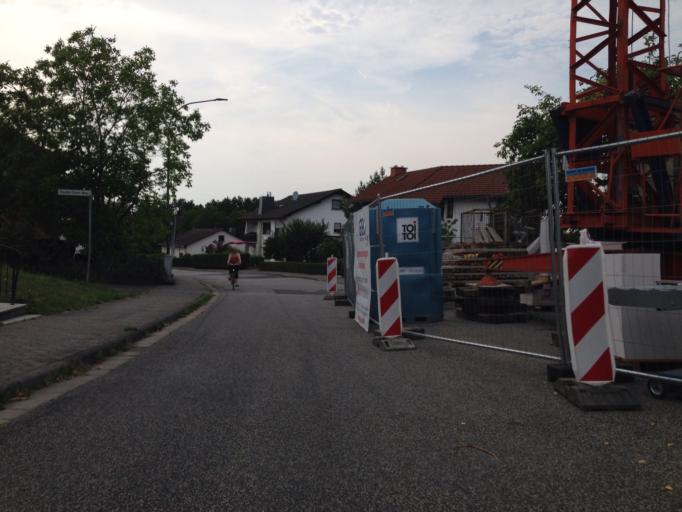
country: DE
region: Hesse
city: Allendorf an der Lahn
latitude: 50.5571
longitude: 8.6411
